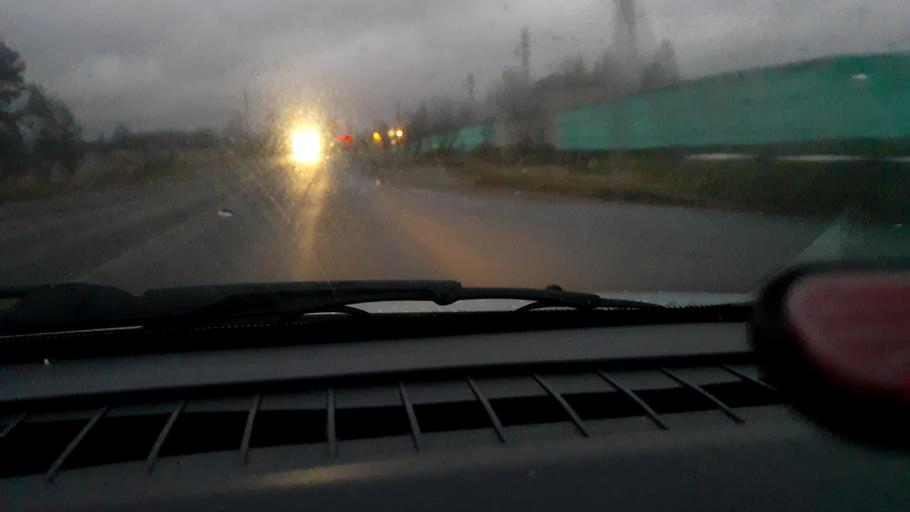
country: RU
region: Nizjnij Novgorod
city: Uren'
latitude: 57.4448
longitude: 45.7301
